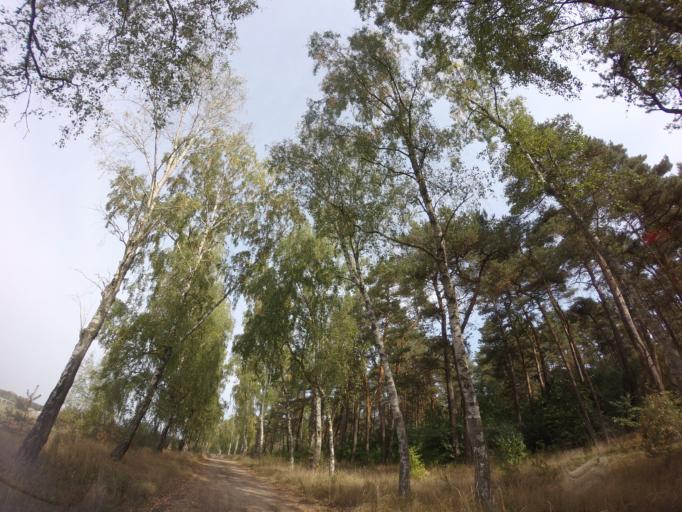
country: PL
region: West Pomeranian Voivodeship
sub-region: Powiat drawski
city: Drawsko Pomorskie
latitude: 53.4622
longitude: 15.7144
